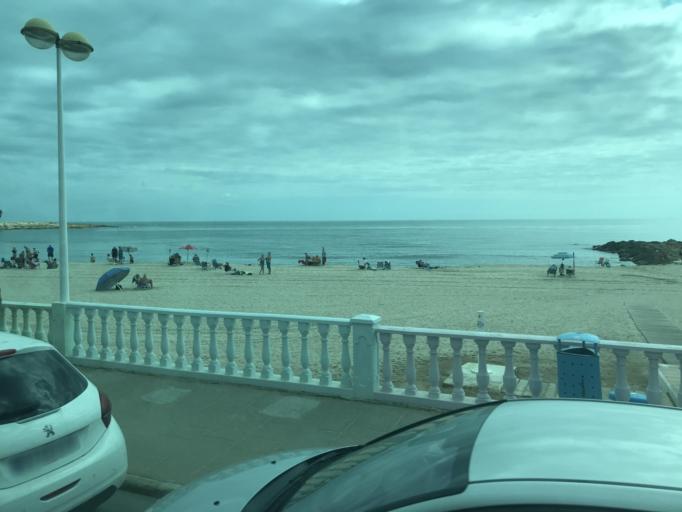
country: ES
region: Valencia
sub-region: Provincia de Alicante
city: Torrevieja
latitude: 37.9819
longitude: -0.6621
